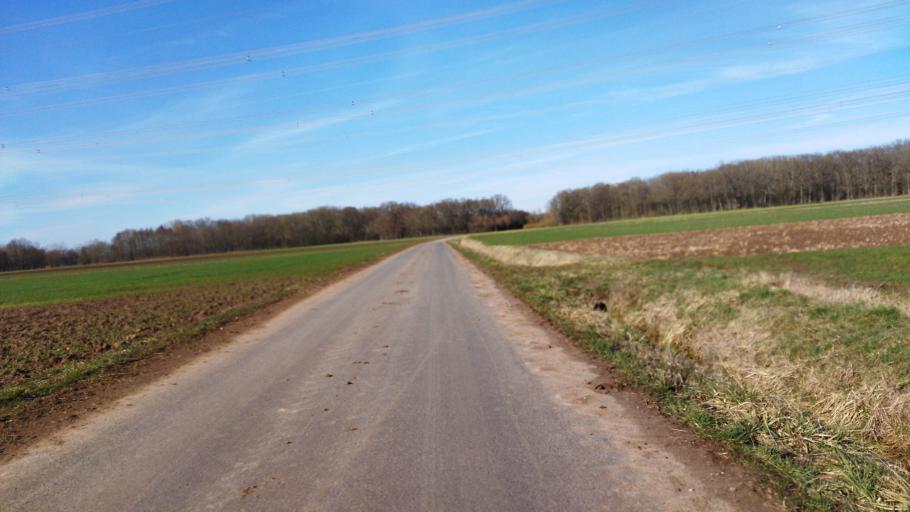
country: DE
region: Bavaria
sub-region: Regierungsbezirk Unterfranken
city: Rothlein
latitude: 49.9770
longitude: 10.1980
